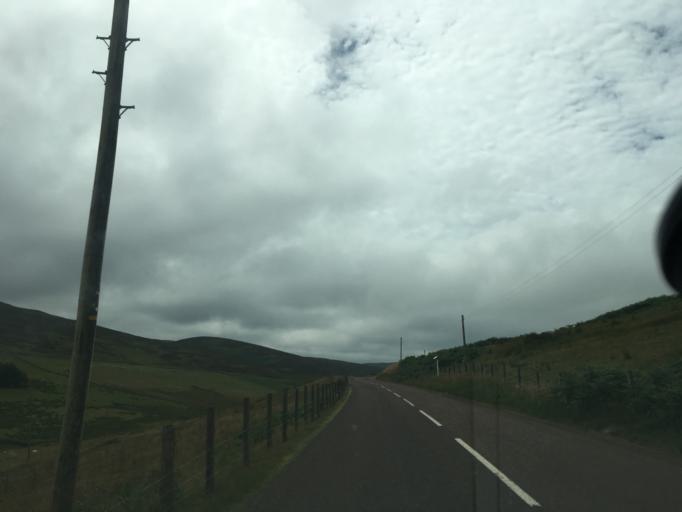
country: GB
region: Scotland
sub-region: South Lanarkshire
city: Douglas
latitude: 55.4792
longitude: -3.7092
